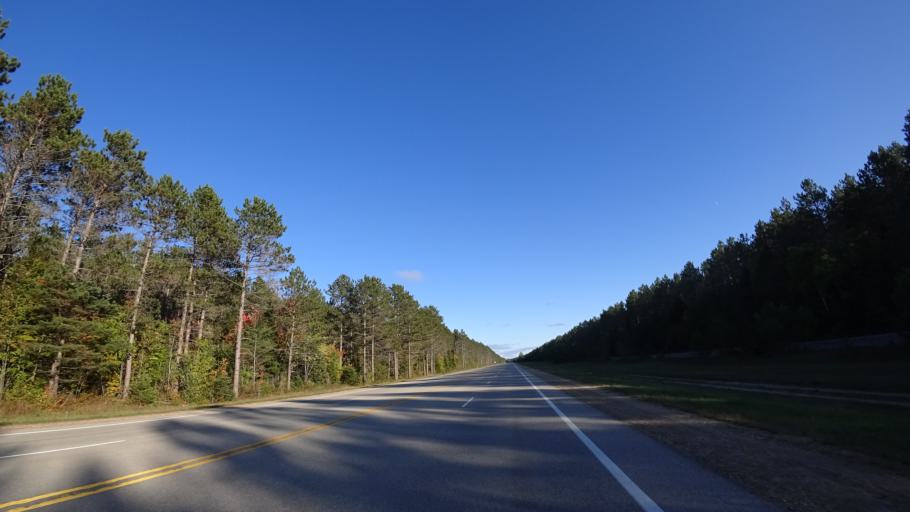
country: US
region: Michigan
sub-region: Alger County
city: Munising
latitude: 46.3599
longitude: -86.5200
